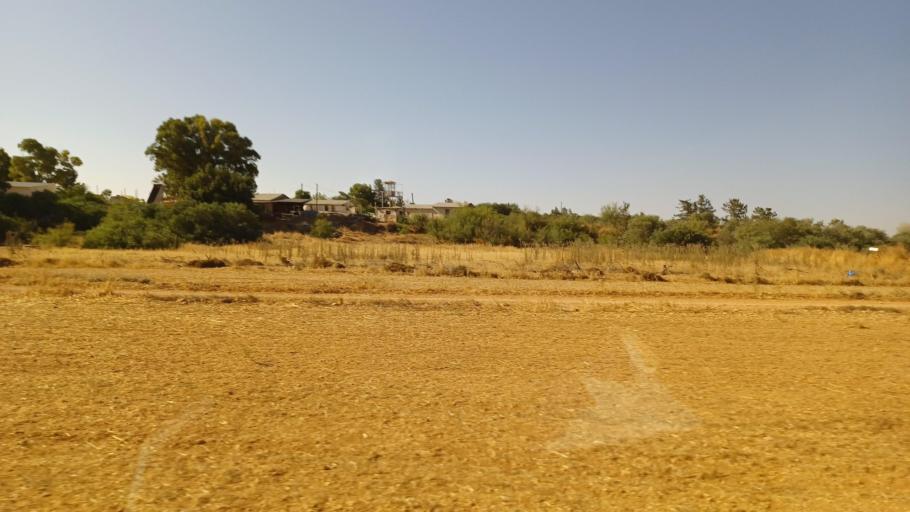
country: CY
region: Larnaka
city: Pergamos
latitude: 35.0488
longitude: 33.7033
